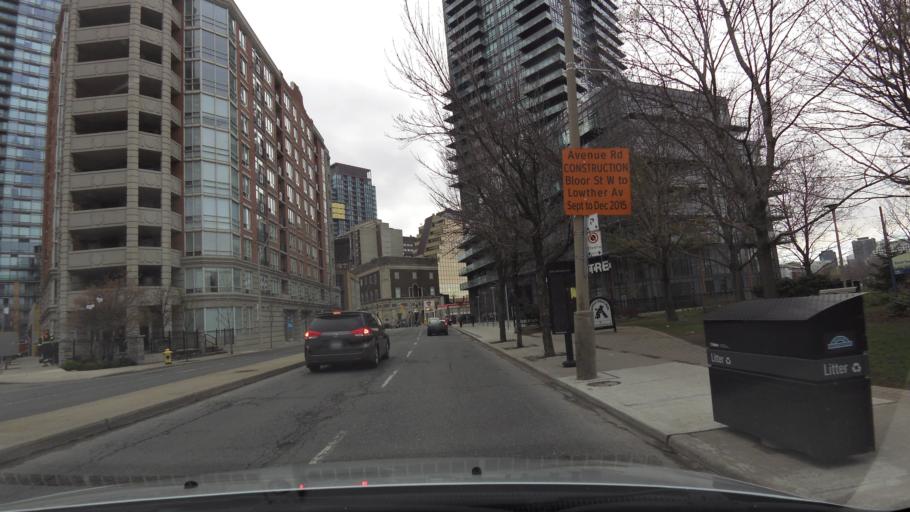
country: CA
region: Ontario
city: Toronto
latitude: 43.6725
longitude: -79.3862
